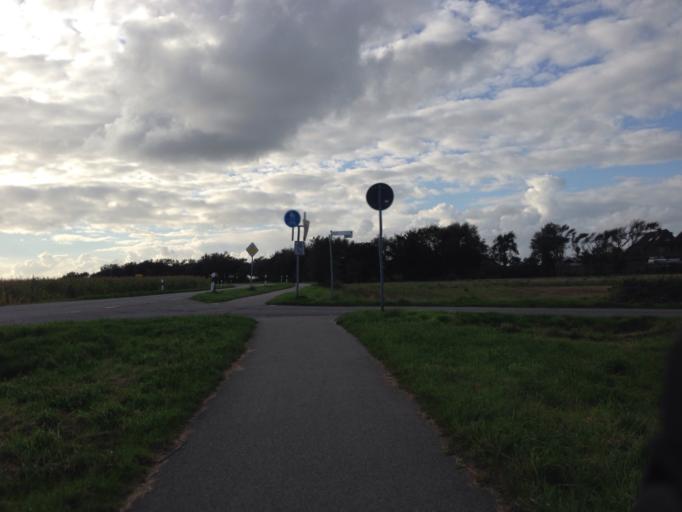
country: DE
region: Schleswig-Holstein
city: Oldsum
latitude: 54.7290
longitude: 8.4472
